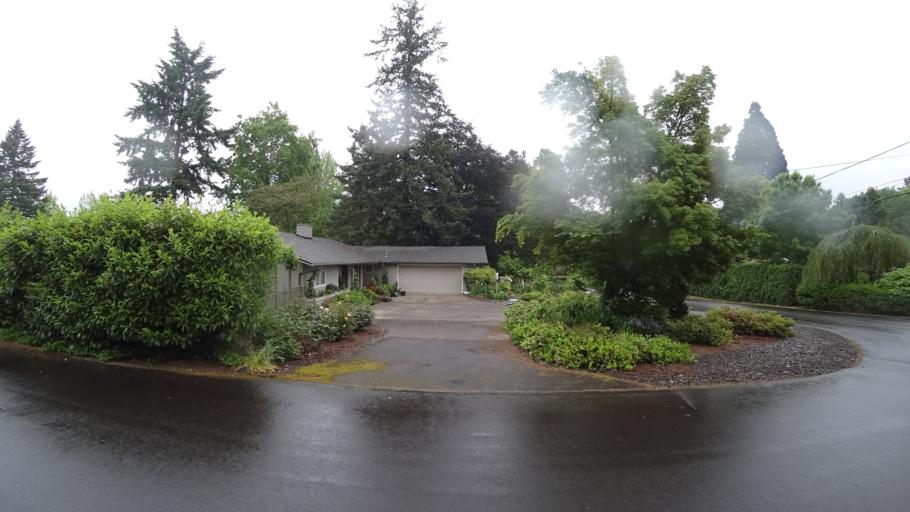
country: US
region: Oregon
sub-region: Washington County
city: Raleigh Hills
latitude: 45.4792
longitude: -122.7694
